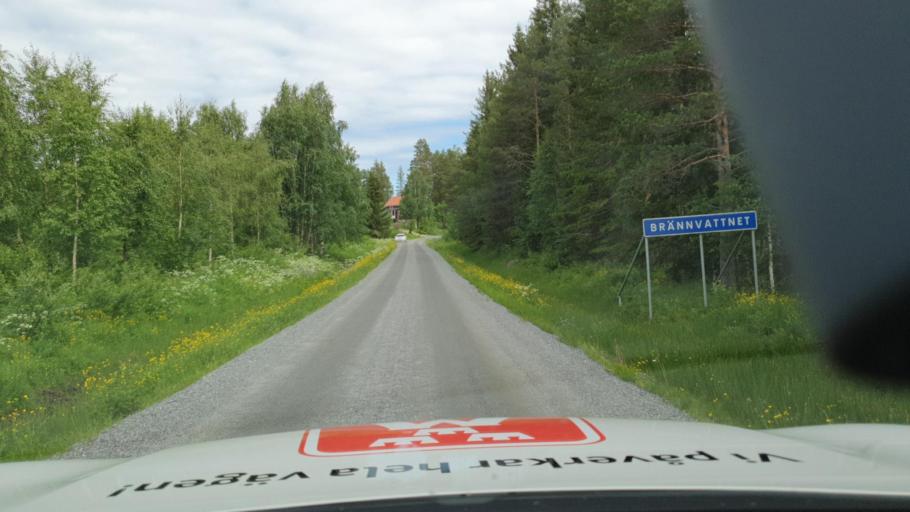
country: SE
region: Vaesterbotten
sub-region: Skelleftea Kommun
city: Langsele
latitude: 64.5660
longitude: 20.2928
